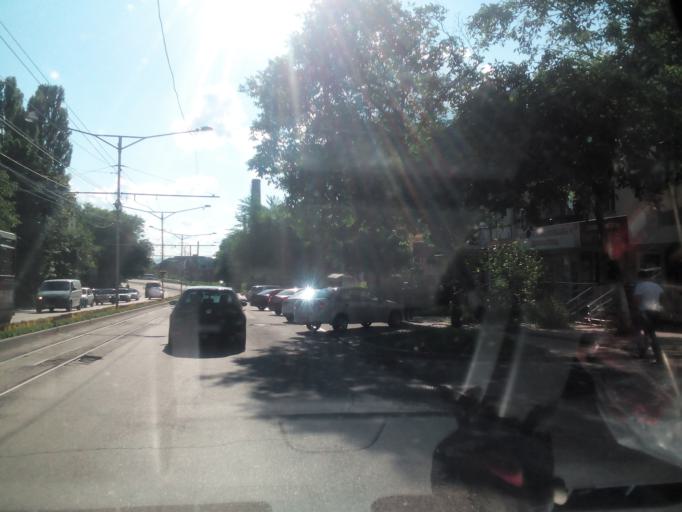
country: RU
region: Stavropol'skiy
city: Pyatigorsk
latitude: 44.0531
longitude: 43.0590
